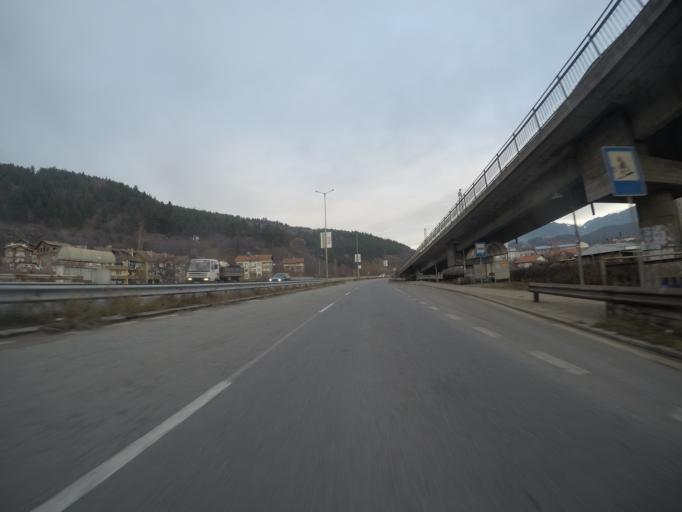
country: BG
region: Kyustendil
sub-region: Obshtina Dupnitsa
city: Dupnitsa
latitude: 42.2679
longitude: 23.1116
